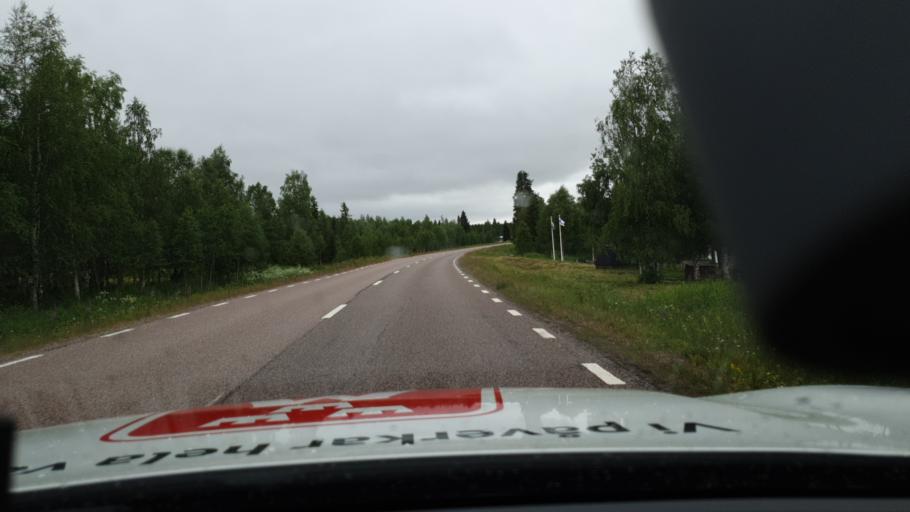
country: FI
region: Lapland
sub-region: Torniolaakso
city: Pello
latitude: 66.9596
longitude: 23.8283
